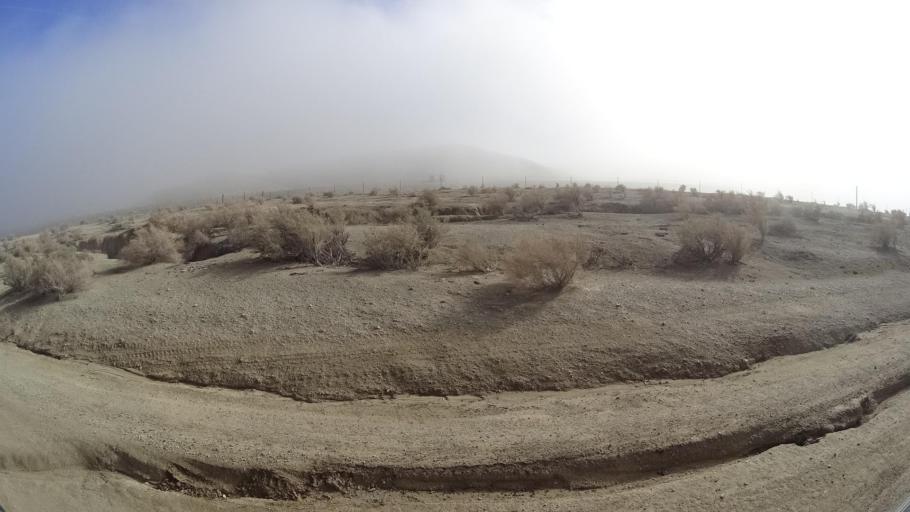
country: US
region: California
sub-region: Kern County
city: Maricopa
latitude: 35.0201
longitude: -119.4488
